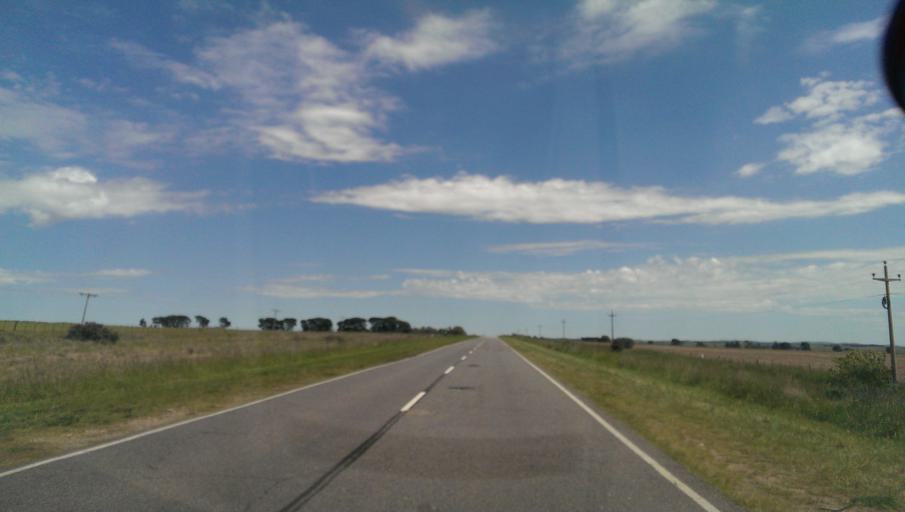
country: AR
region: Buenos Aires
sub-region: Partido de Tornquist
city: Tornquist
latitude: -38.0612
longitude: -62.2009
